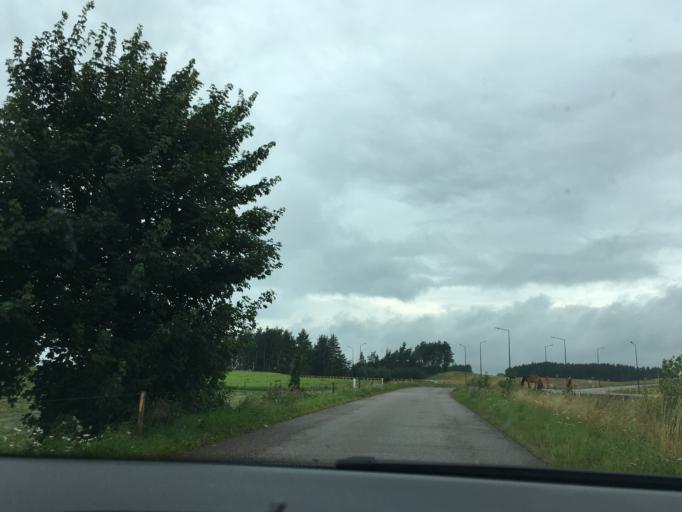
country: PL
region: Podlasie
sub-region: Powiat sejnenski
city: Krasnopol
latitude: 54.0976
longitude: 23.2215
